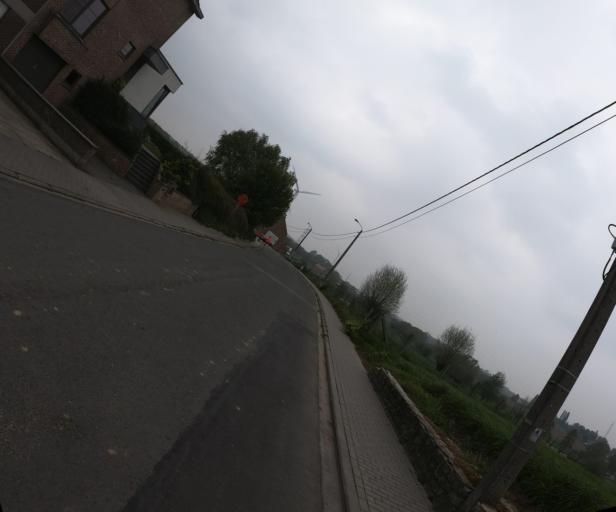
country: BE
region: Flanders
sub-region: Provincie Vlaams-Brabant
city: Halle
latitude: 50.7324
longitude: 4.2224
